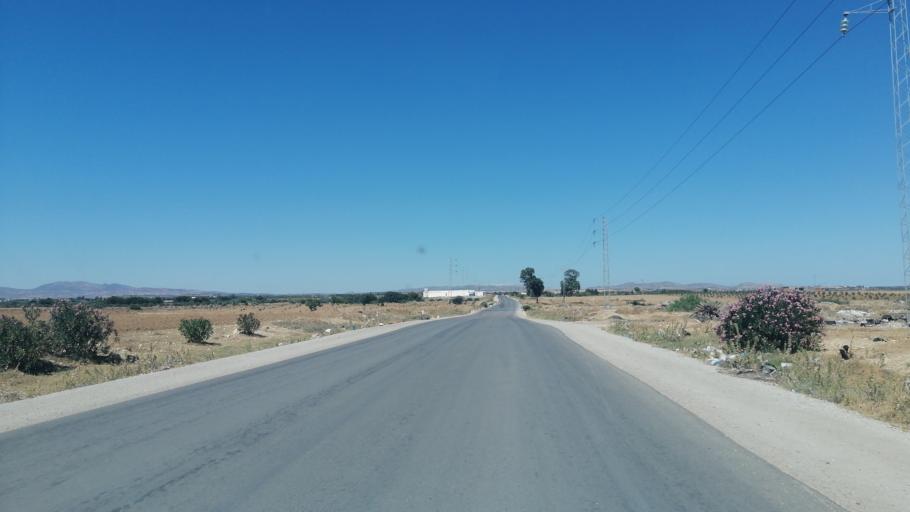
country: TN
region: Al Qayrawan
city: Sbikha
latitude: 36.1269
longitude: 10.0990
